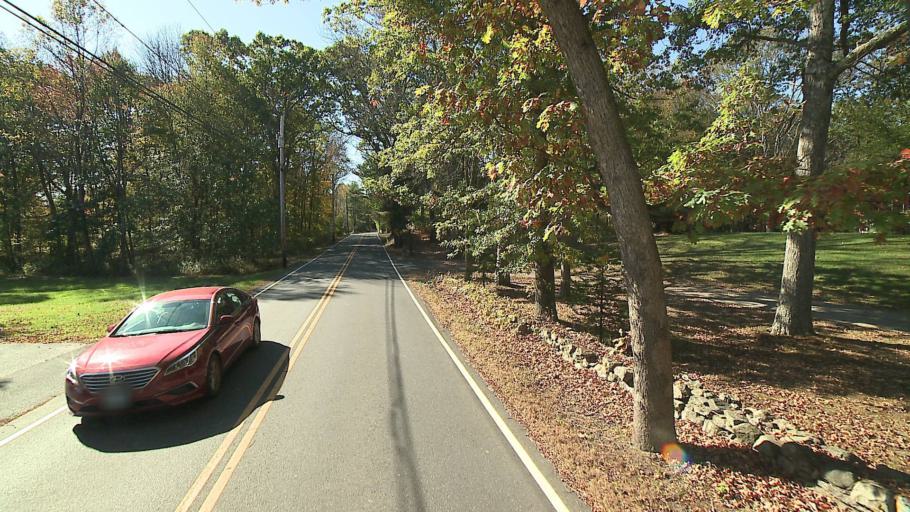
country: US
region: Connecticut
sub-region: Fairfield County
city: Trumbull
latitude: 41.2587
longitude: -73.3008
